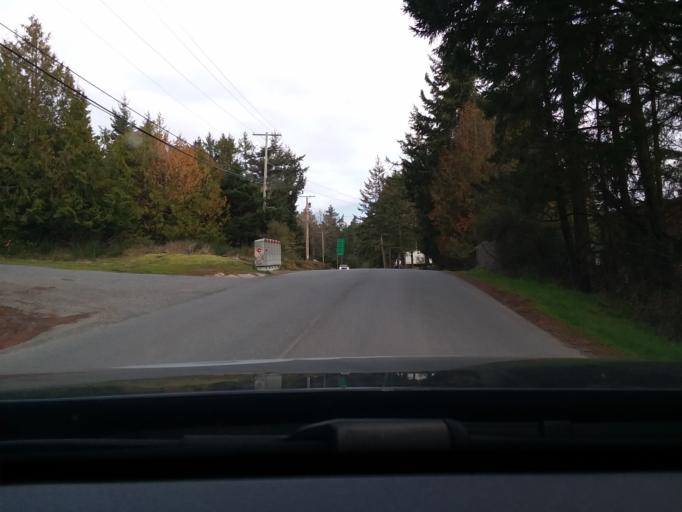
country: CA
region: British Columbia
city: North Saanich
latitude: 48.8759
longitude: -123.3218
